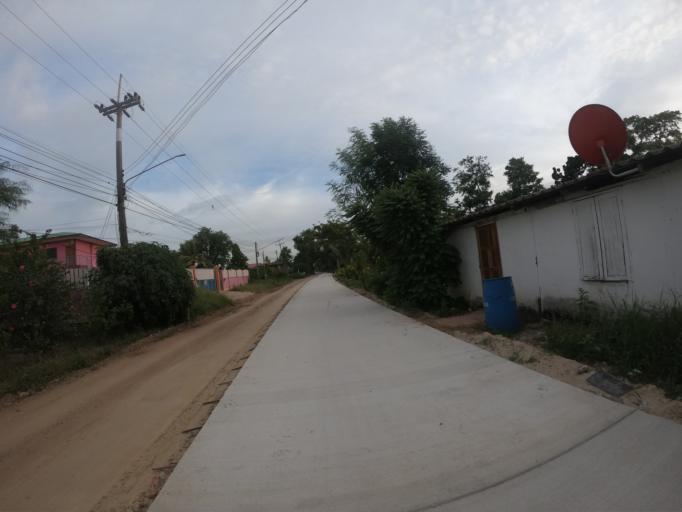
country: TH
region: Pathum Thani
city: Ban Lam Luk Ka
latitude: 14.0148
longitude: 100.7994
